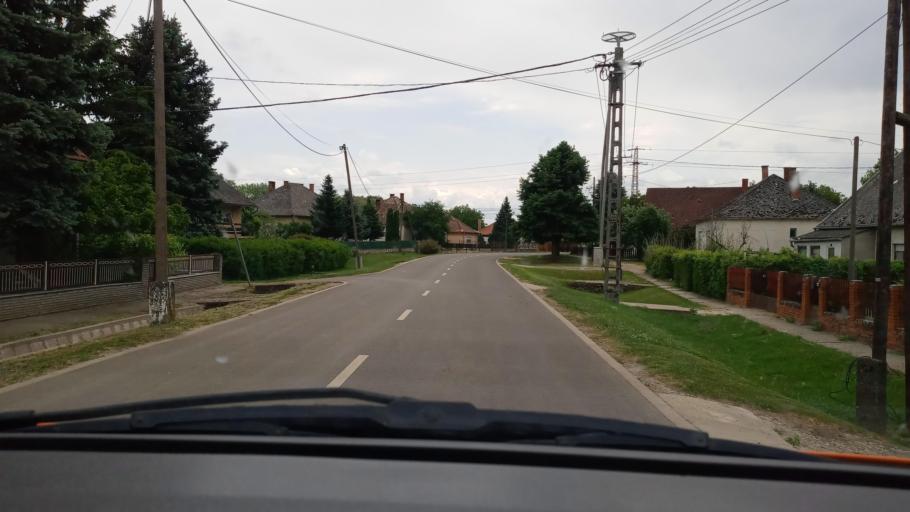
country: HU
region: Baranya
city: Vajszlo
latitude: 45.8559
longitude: 17.9825
